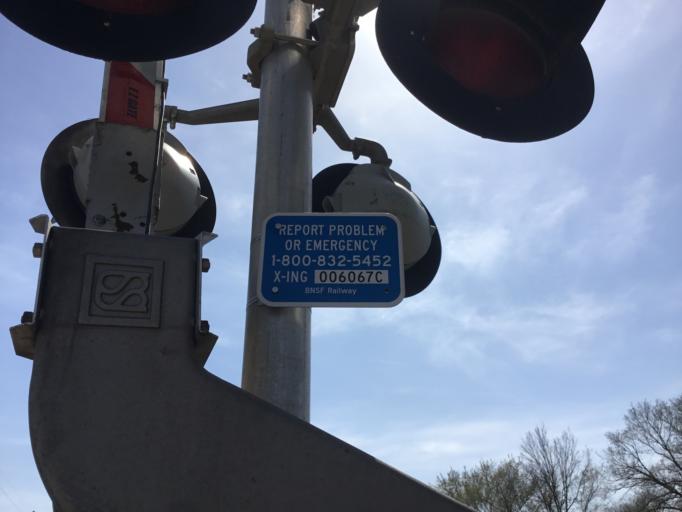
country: US
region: Kansas
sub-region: Lyon County
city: Emporia
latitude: 38.4014
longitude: -96.1710
